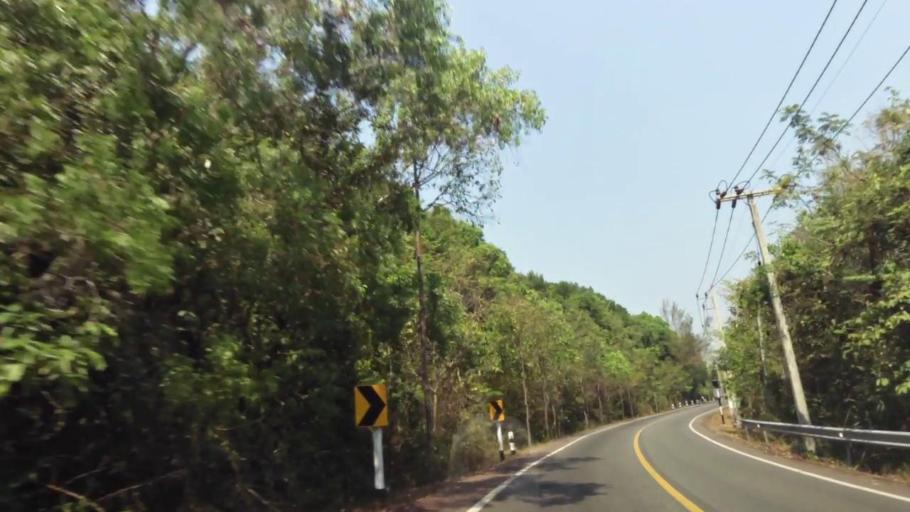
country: TH
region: Chanthaburi
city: Tha Mai
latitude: 12.5340
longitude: 101.9474
